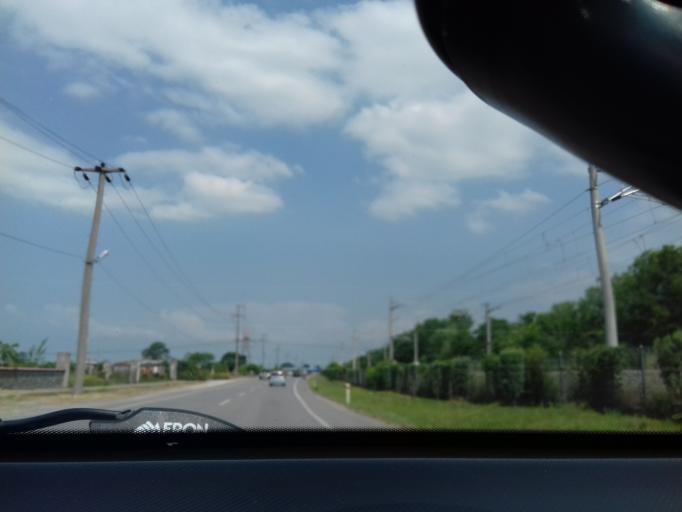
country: TR
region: Sakarya
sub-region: Merkez
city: Sapanca
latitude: 40.7128
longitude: 30.3288
